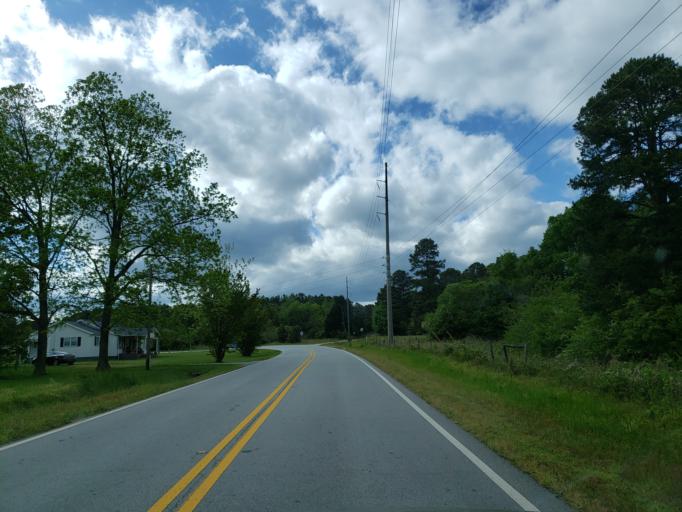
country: US
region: Georgia
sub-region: Carroll County
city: Mount Zion
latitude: 33.6698
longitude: -85.2575
